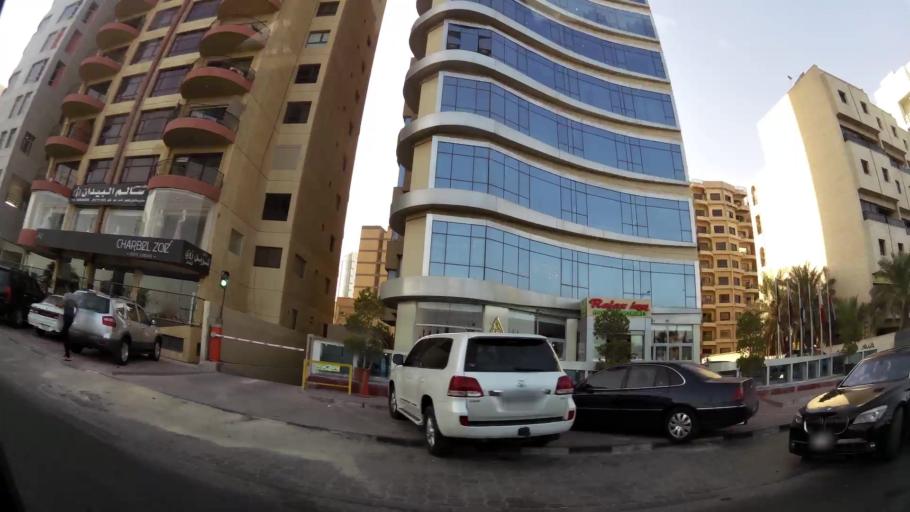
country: KW
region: Muhafazat Hawalli
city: As Salimiyah
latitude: 29.3353
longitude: 48.0938
